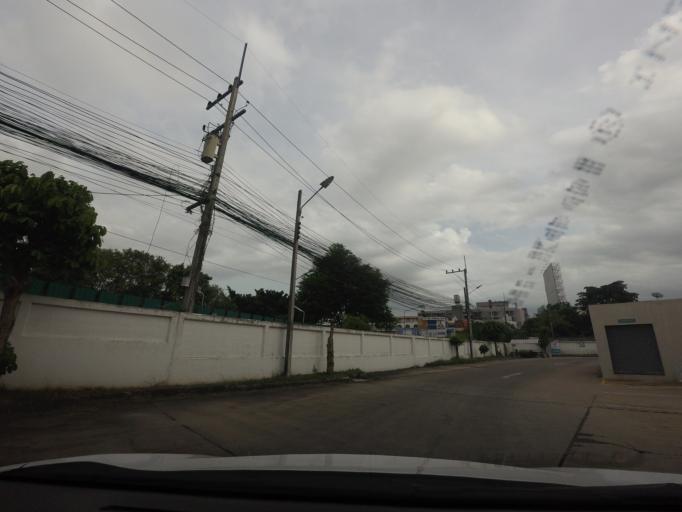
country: TH
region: Chon Buri
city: Phatthaya
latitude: 12.9513
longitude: 100.8947
